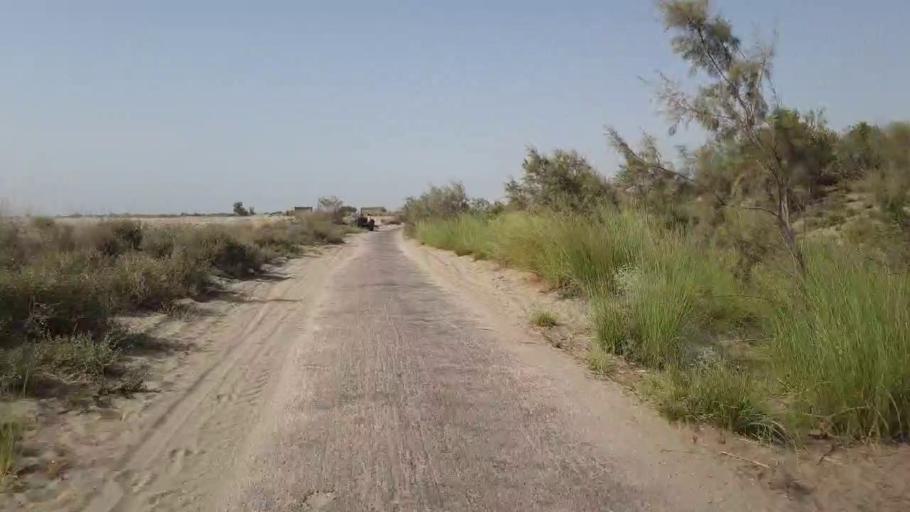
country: PK
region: Sindh
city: Jam Sahib
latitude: 26.5976
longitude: 68.9235
